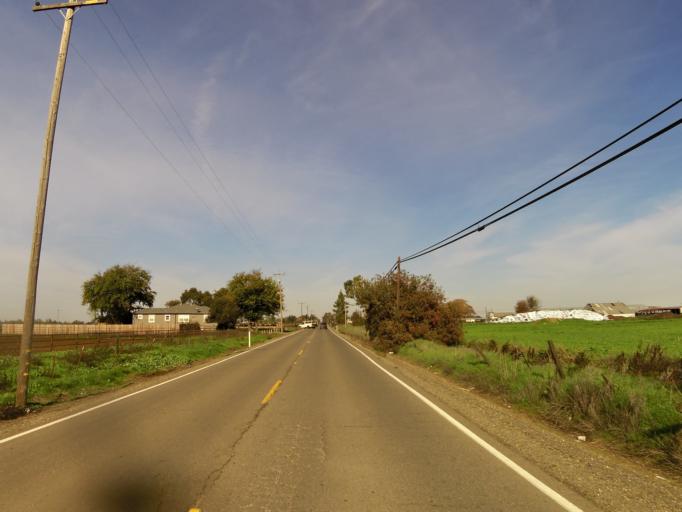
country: US
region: California
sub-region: Sacramento County
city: Elk Grove
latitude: 38.3260
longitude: -121.4172
